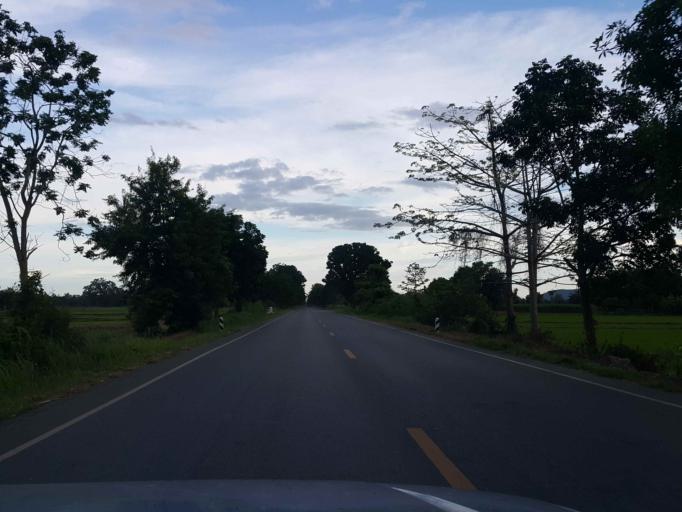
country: TH
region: Sukhothai
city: Sawankhalok
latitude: 17.3653
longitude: 99.7417
